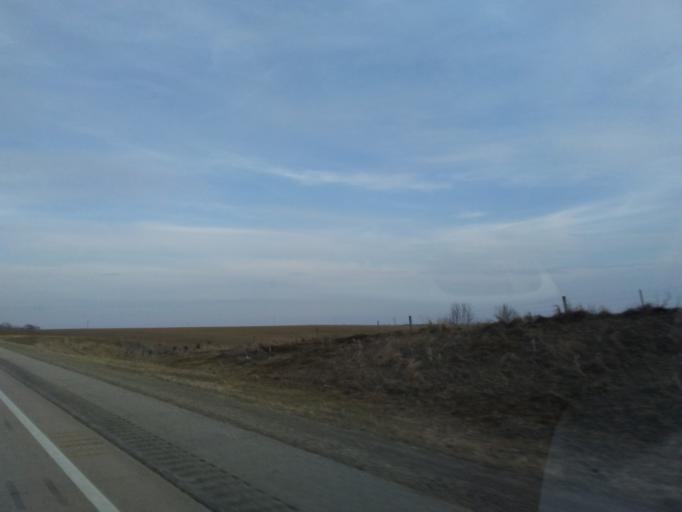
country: US
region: Wisconsin
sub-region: Iowa County
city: Barneveld
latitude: 43.0095
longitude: -89.9335
